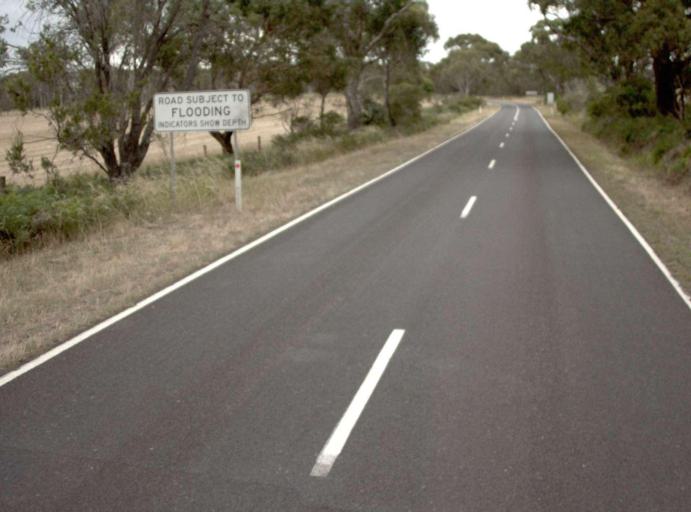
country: AU
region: Victoria
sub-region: East Gippsland
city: Bairnsdale
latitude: -37.9794
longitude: 147.4162
